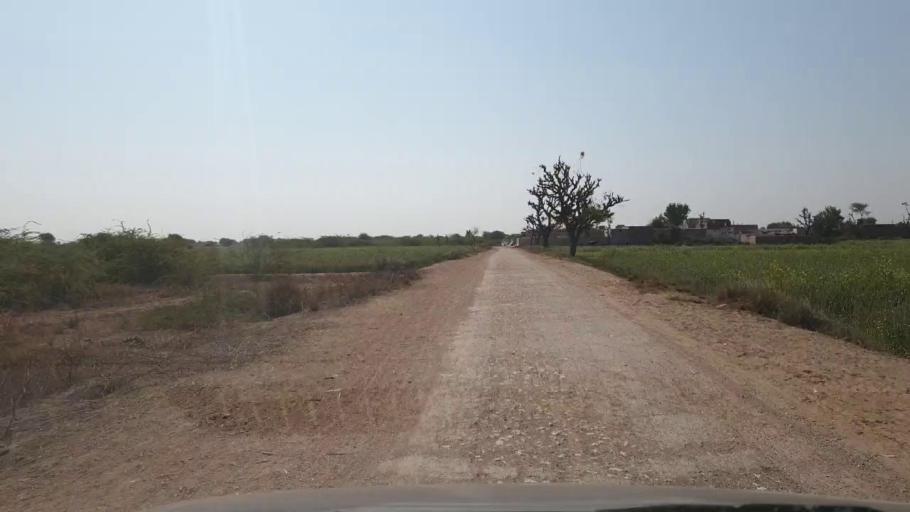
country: PK
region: Sindh
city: Digri
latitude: 25.1844
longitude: 69.2168
